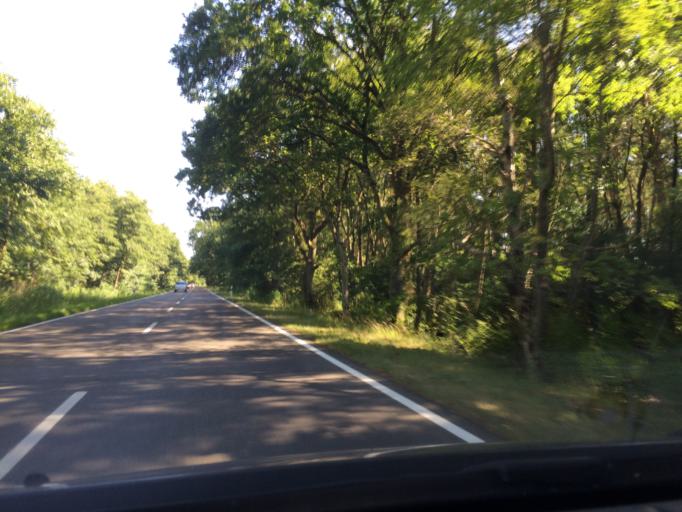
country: DE
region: Mecklenburg-Vorpommern
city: Zingst
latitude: 54.4384
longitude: 12.6492
